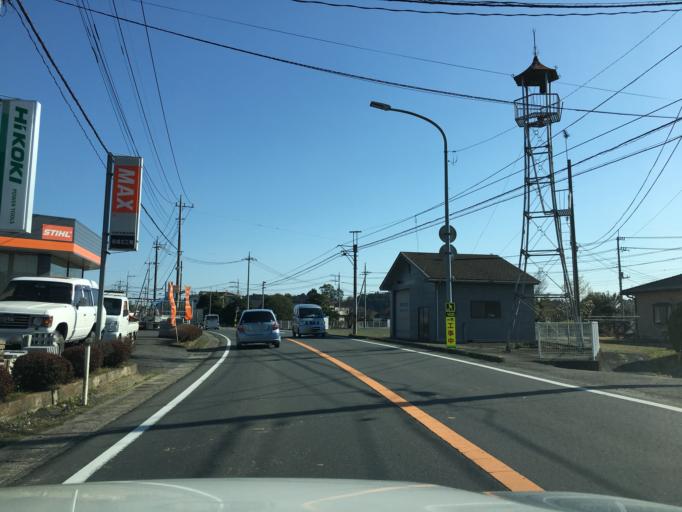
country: JP
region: Ibaraki
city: Omiya
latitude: 36.4970
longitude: 140.3720
